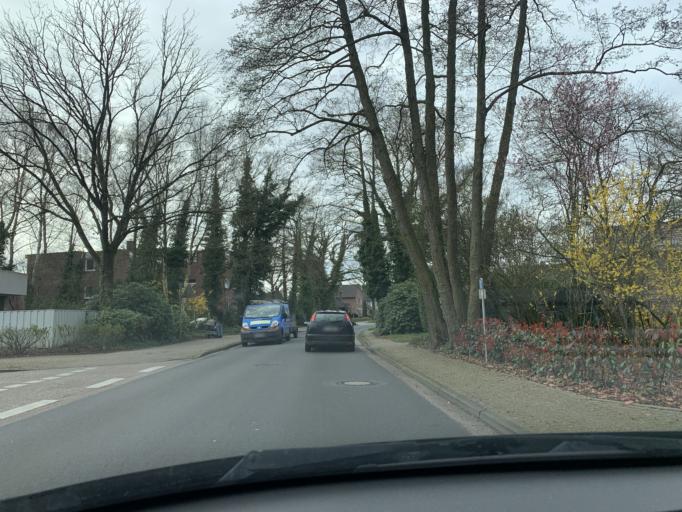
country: DE
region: Lower Saxony
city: Oldenburg
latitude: 53.1273
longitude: 8.1843
